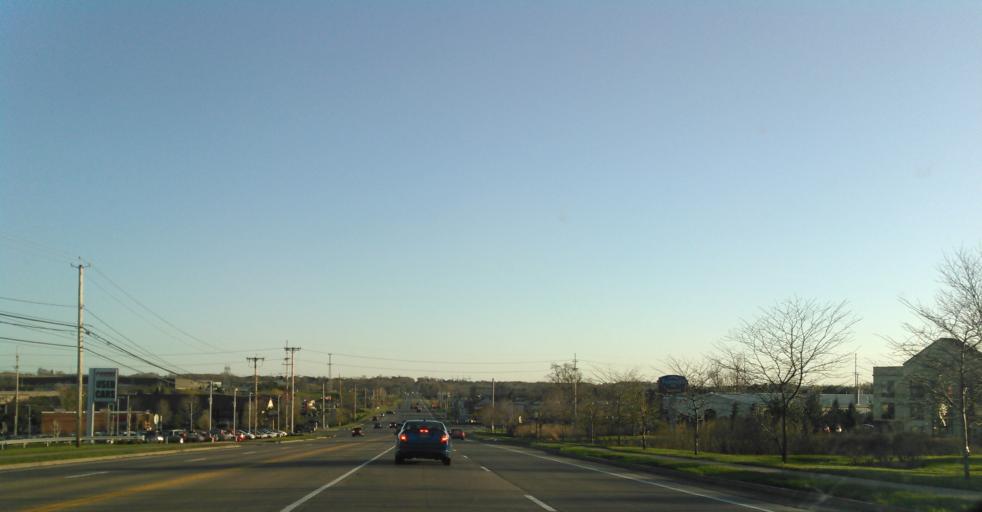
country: US
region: New York
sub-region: Monroe County
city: Scottsville
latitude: 43.0605
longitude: -77.6512
